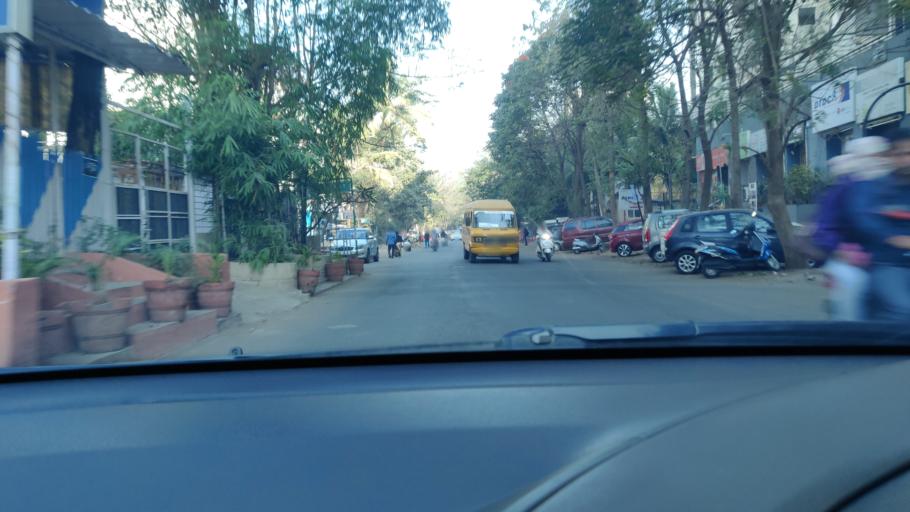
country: IN
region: Maharashtra
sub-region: Pune Division
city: Khadki
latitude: 18.5639
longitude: 73.8026
